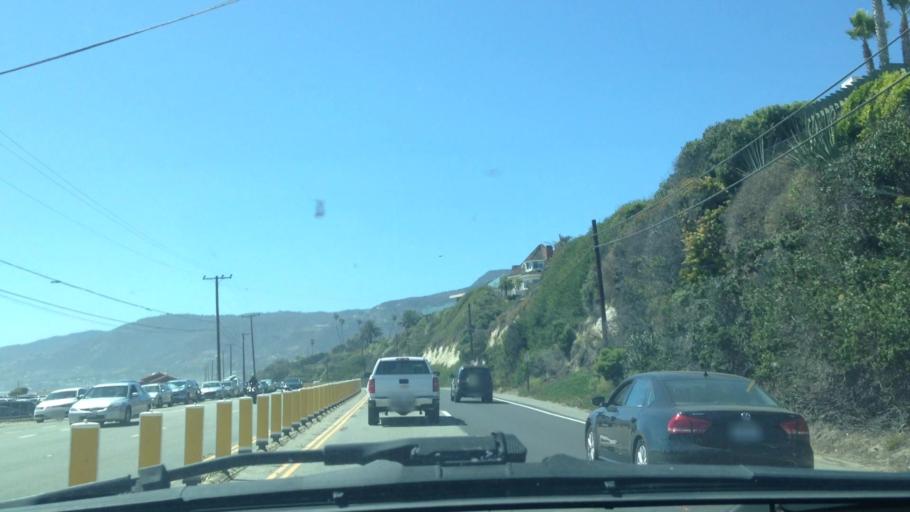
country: US
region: California
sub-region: Los Angeles County
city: Malibu
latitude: 34.0218
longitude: -118.8297
